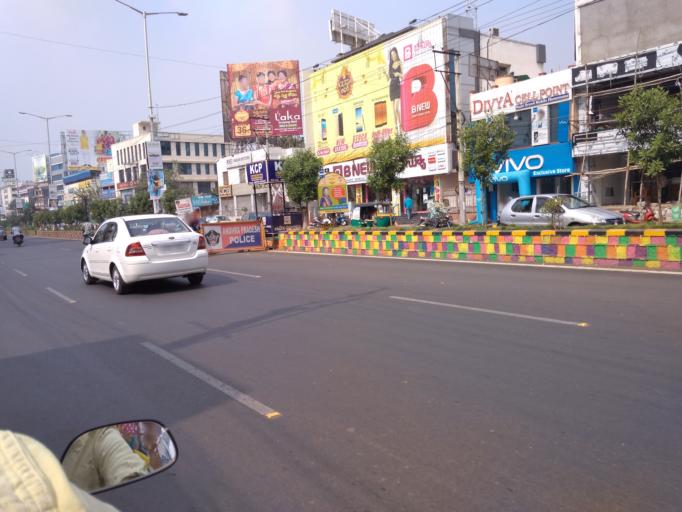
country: IN
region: Andhra Pradesh
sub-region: Krishna
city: Yanamalakuduru
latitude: 16.4987
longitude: 80.6512
